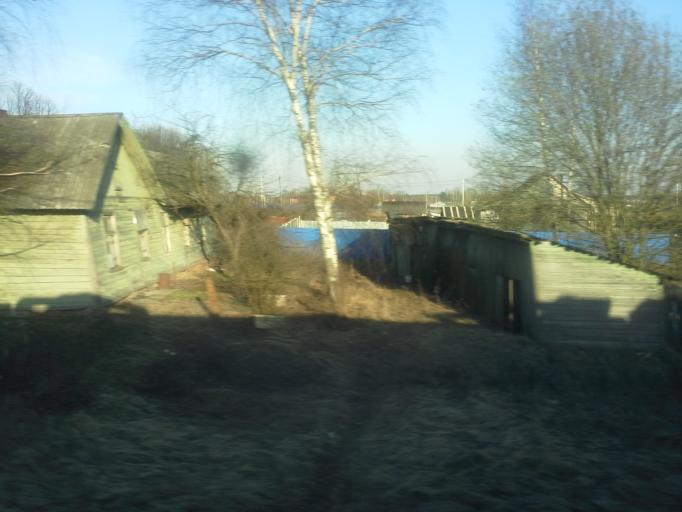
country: RU
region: Moskovskaya
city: Nekrasovskiy
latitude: 56.0851
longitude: 37.5015
